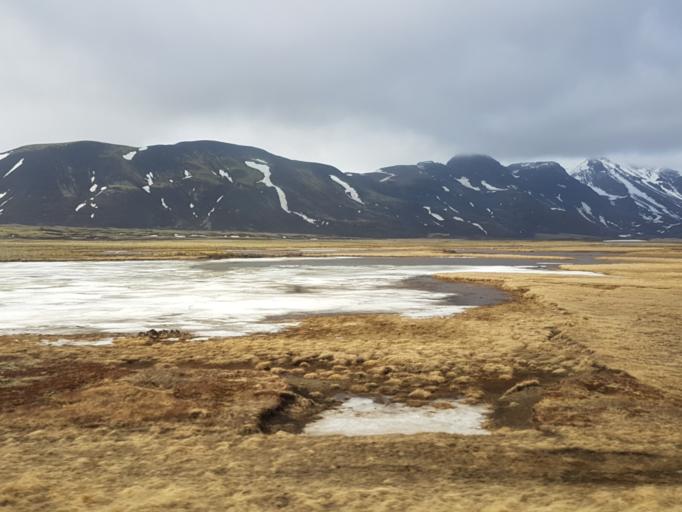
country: IS
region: South
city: Selfoss
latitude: 64.1978
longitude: -20.8796
